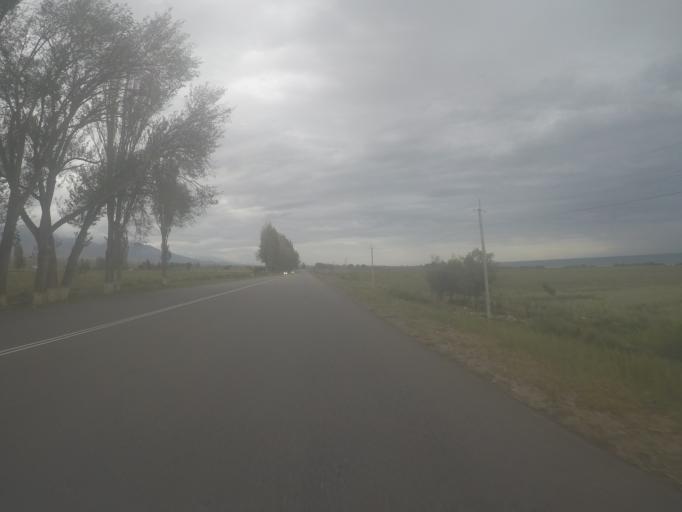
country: KG
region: Ysyk-Koel
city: Cholpon-Ata
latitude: 42.5966
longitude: 76.7766
